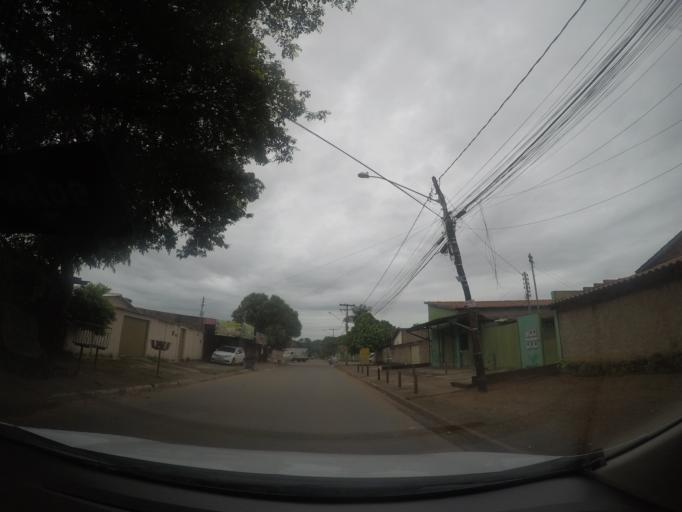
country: BR
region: Goias
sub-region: Goiania
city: Goiania
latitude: -16.6905
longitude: -49.3332
